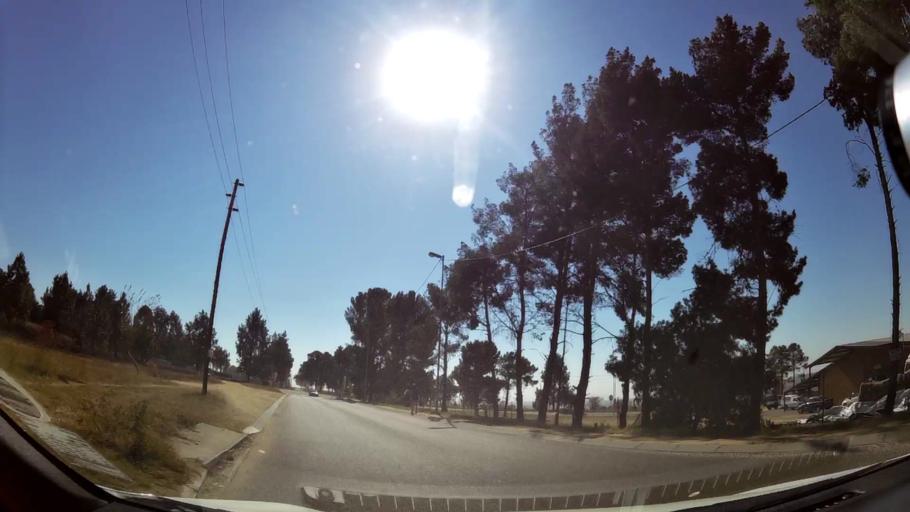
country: ZA
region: Gauteng
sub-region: City of Johannesburg Metropolitan Municipality
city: Midrand
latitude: -25.9417
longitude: 28.1000
